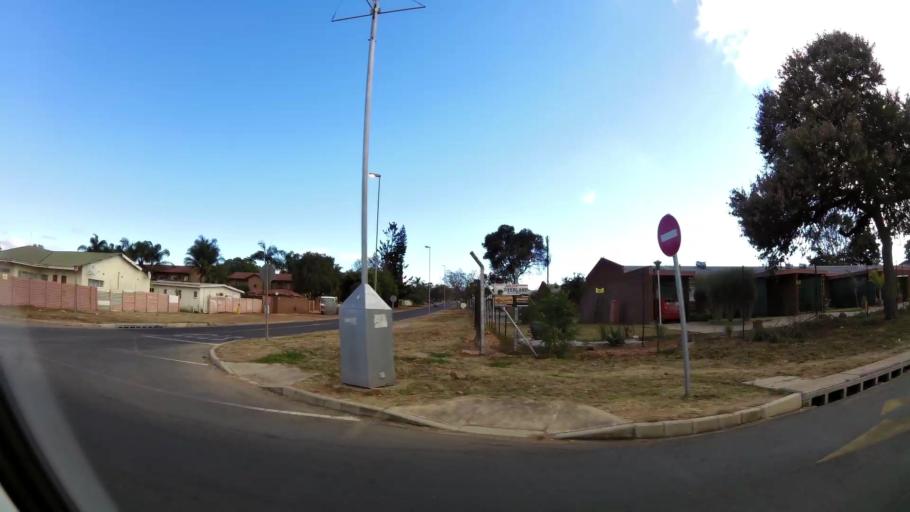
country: ZA
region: Limpopo
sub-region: Capricorn District Municipality
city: Polokwane
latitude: -23.9175
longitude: 29.4690
